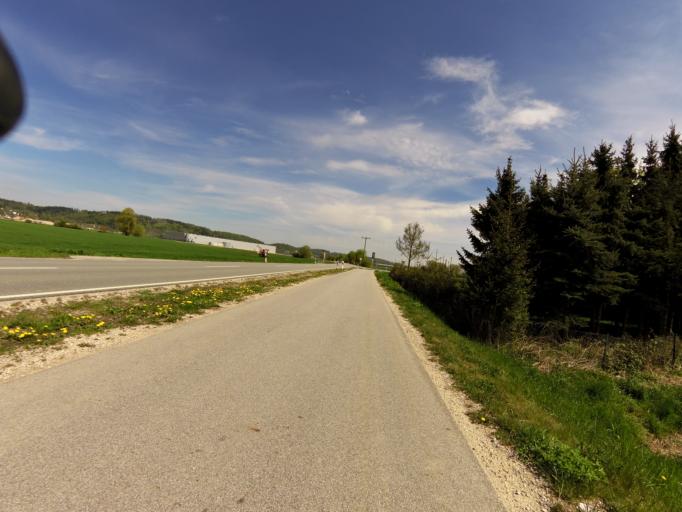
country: DE
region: Bavaria
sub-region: Lower Bavaria
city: Eching
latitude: 48.5241
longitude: 12.0589
